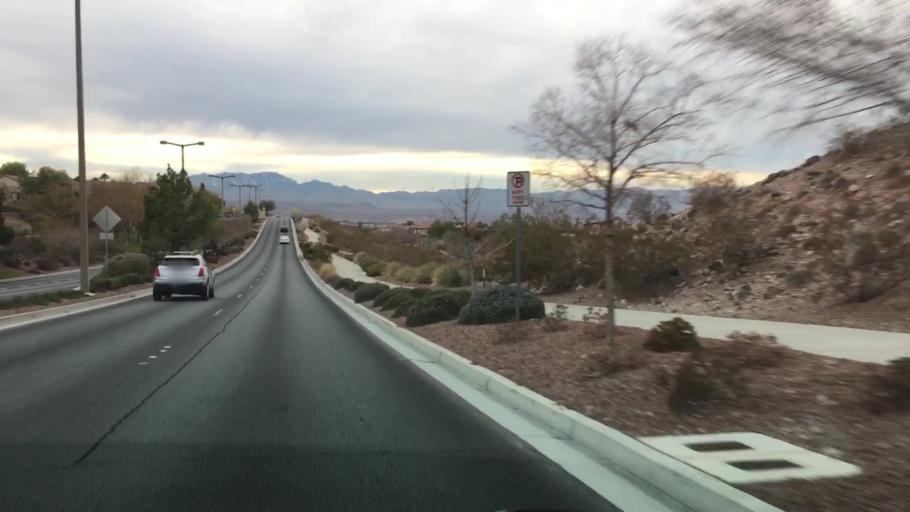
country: US
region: Nevada
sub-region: Clark County
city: Whitney
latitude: 35.9694
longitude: -115.1047
